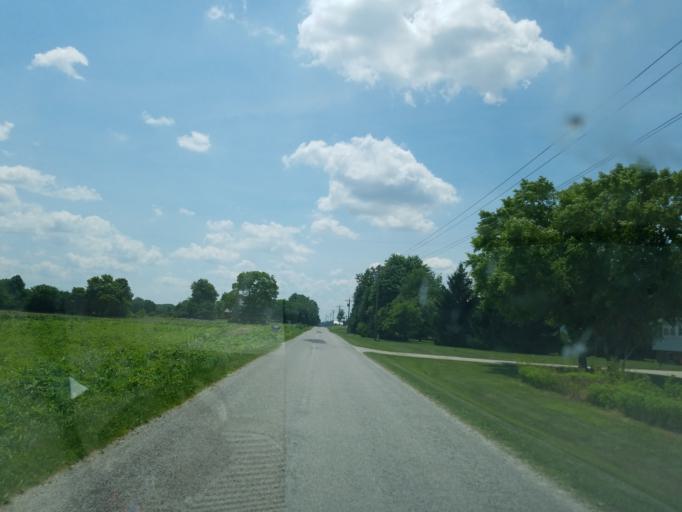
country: US
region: Ohio
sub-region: Marion County
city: Marion
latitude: 40.6251
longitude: -82.9910
